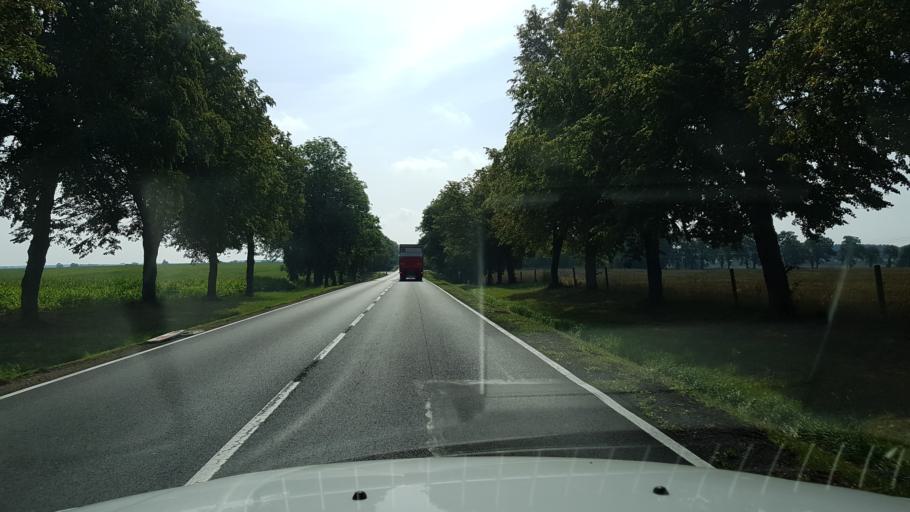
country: PL
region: West Pomeranian Voivodeship
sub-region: Powiat walecki
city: Tuczno
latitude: 53.3373
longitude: 16.2774
